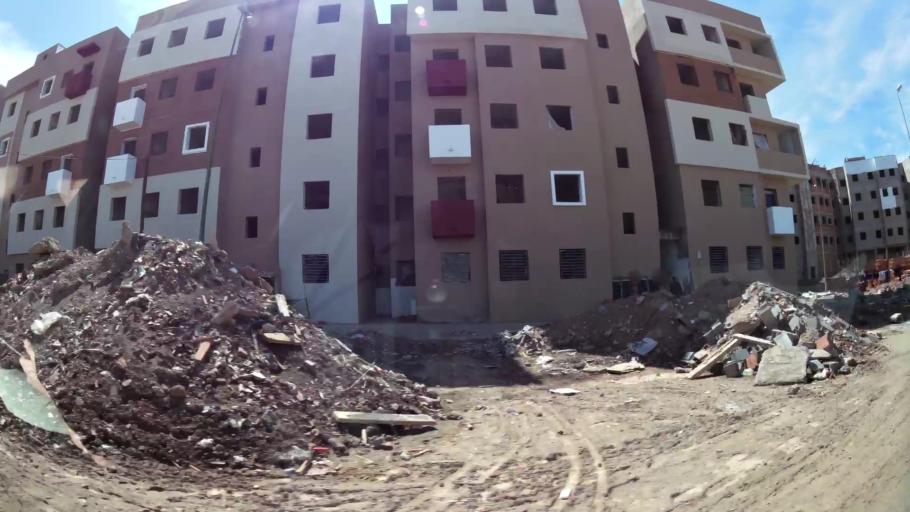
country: MA
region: Marrakech-Tensift-Al Haouz
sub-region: Marrakech
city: Marrakesh
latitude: 31.6327
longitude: -8.0731
